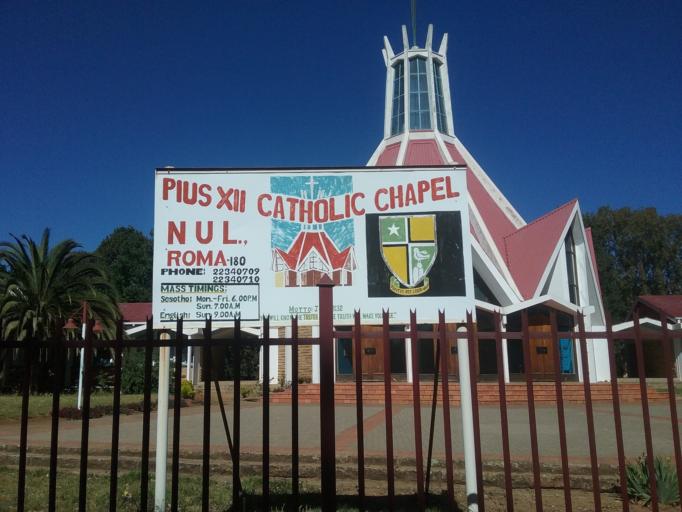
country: LS
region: Maseru
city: Nako
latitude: -29.4498
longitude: 27.7243
